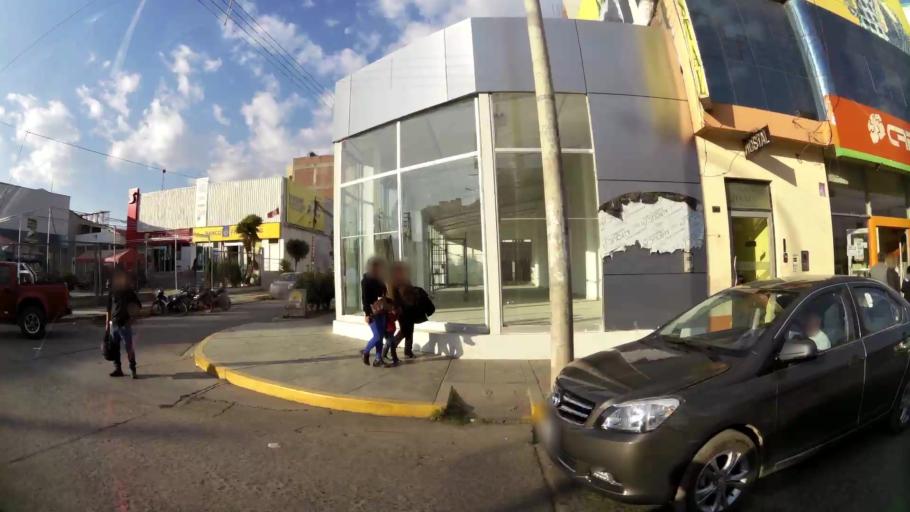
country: PE
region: Junin
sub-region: Provincia de Huancayo
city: El Tambo
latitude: -12.0535
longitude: -75.2196
